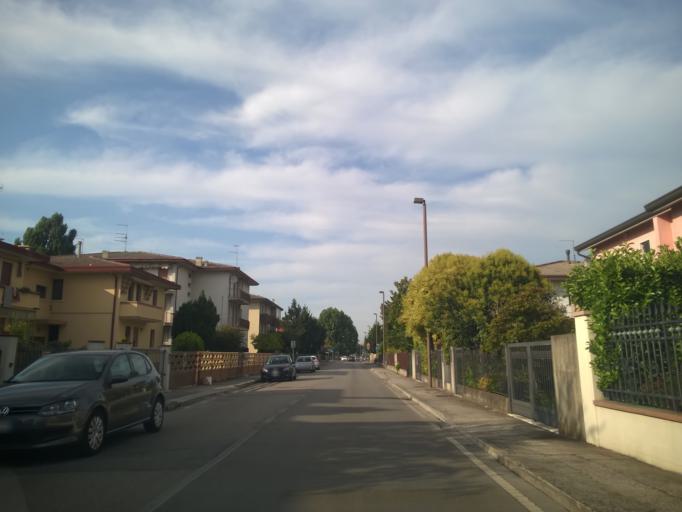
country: IT
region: Veneto
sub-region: Provincia di Padova
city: Piove di Sacco-Piovega
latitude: 45.2892
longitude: 12.0342
